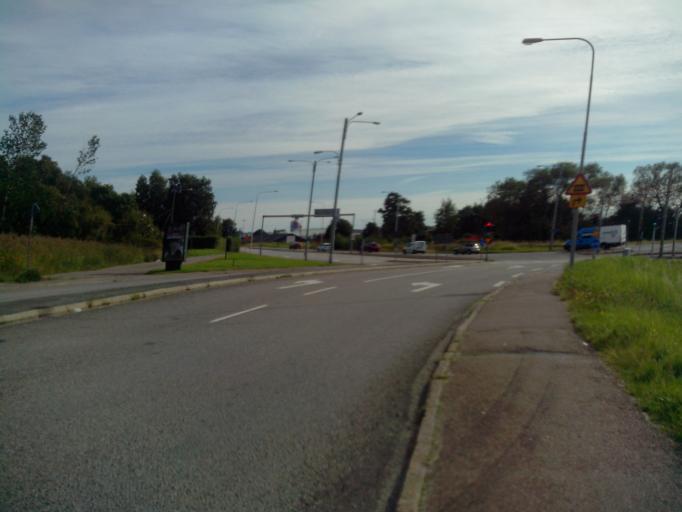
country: SE
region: Vaestra Goetaland
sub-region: Goteborg
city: Goeteborg
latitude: 57.7307
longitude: 11.9593
